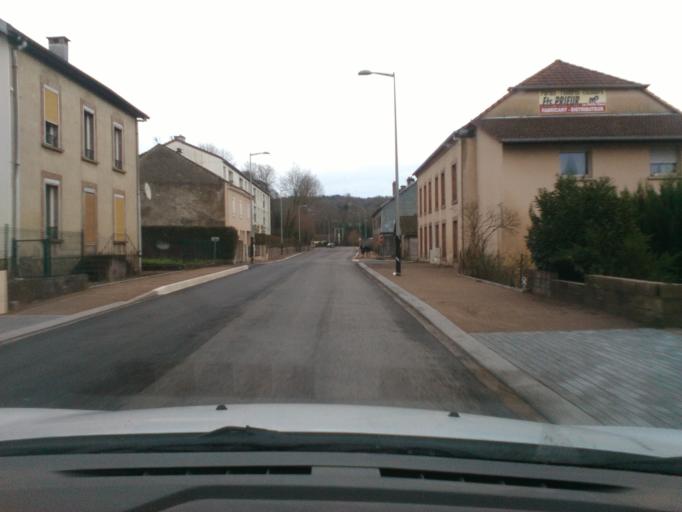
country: FR
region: Lorraine
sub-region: Departement des Vosges
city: Moyenmoutier
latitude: 48.3774
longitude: 6.9034
